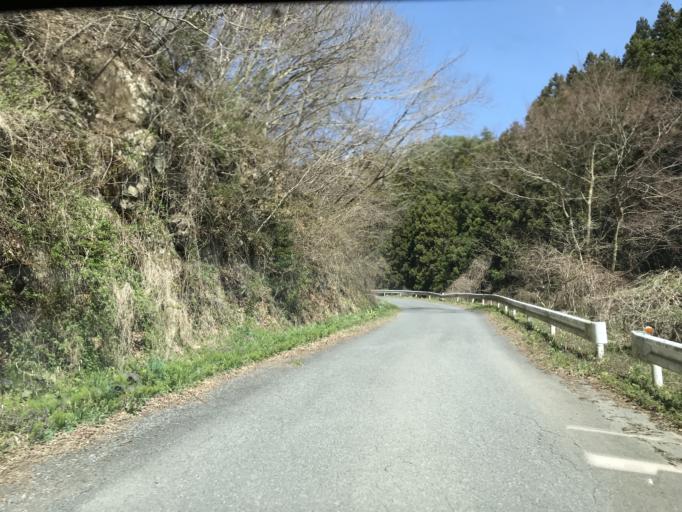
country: JP
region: Iwate
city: Ichinoseki
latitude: 38.8240
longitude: 141.2853
